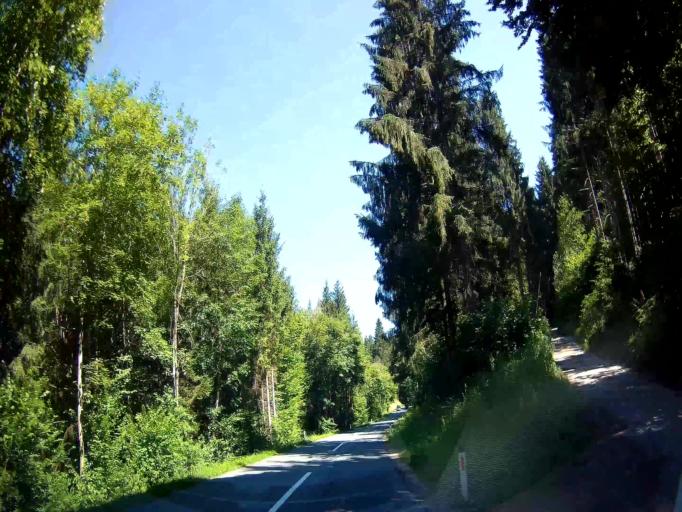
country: AT
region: Carinthia
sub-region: Politischer Bezirk Klagenfurt Land
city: Grafenstein
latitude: 46.6005
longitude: 14.4309
